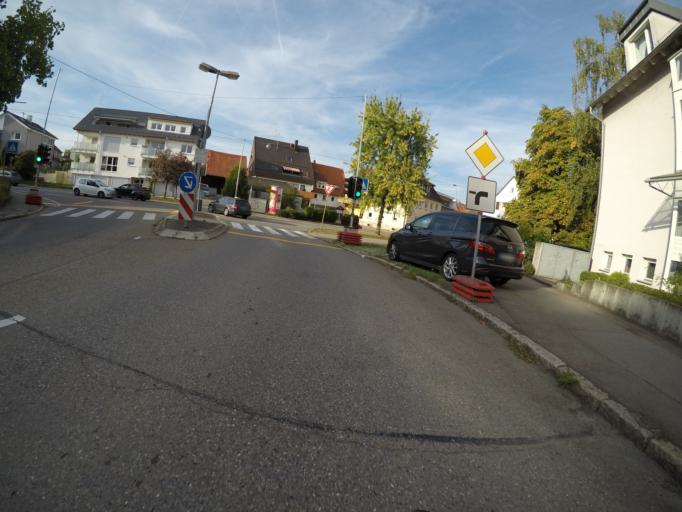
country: DE
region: Baden-Wuerttemberg
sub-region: Regierungsbezirk Stuttgart
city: Denkendorf
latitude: 48.7106
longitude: 9.2940
